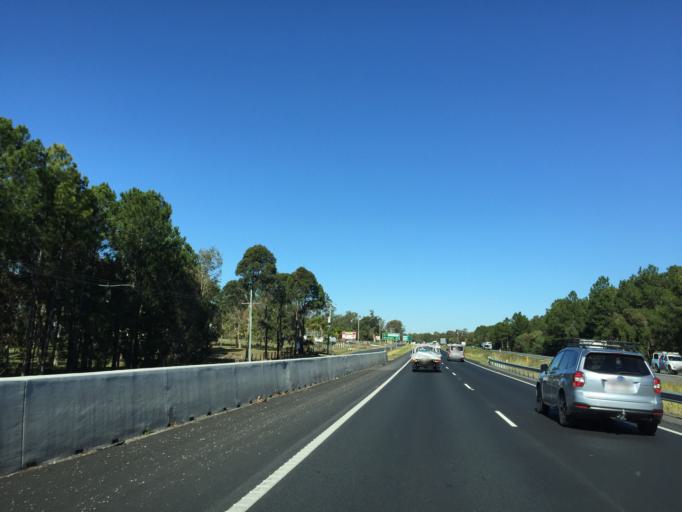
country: AU
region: Queensland
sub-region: Moreton Bay
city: Caboolture
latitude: -27.0479
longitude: 152.9775
